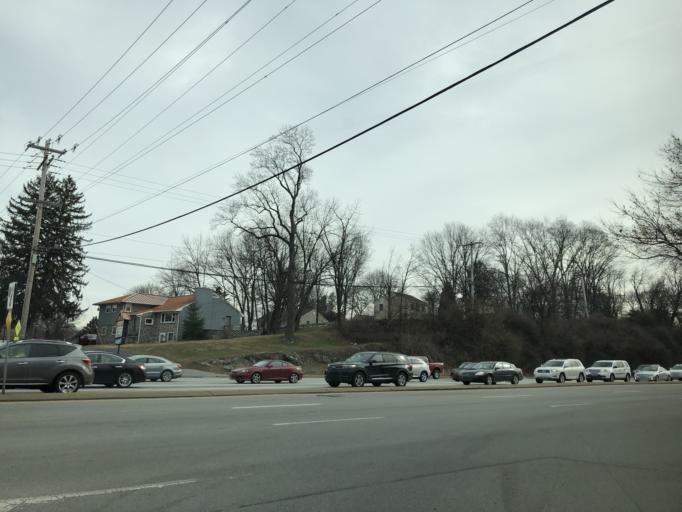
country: US
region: Pennsylvania
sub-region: Chester County
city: Exton
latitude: 40.0260
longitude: -75.6271
